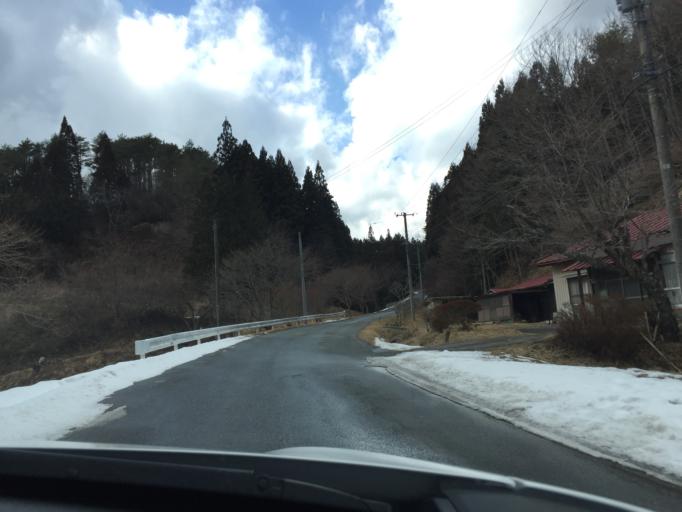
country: JP
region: Fukushima
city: Iwaki
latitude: 37.2275
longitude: 140.7399
